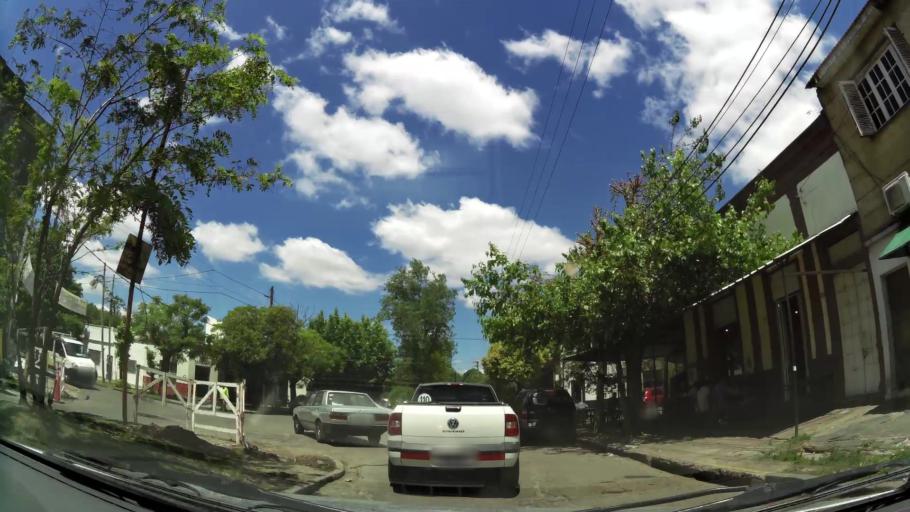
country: AR
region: Buenos Aires
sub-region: Partido de Lanus
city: Lanus
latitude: -34.7281
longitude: -58.4053
